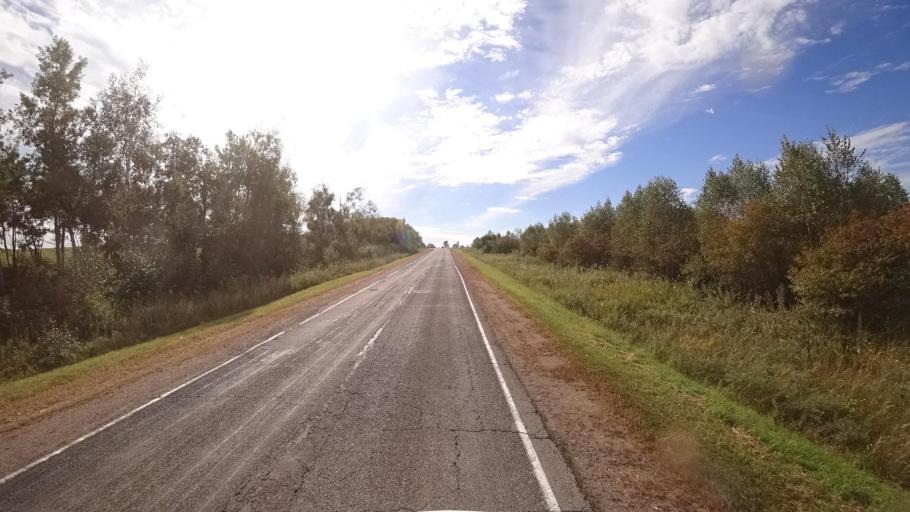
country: RU
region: Primorskiy
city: Dostoyevka
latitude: 44.3253
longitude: 133.4935
